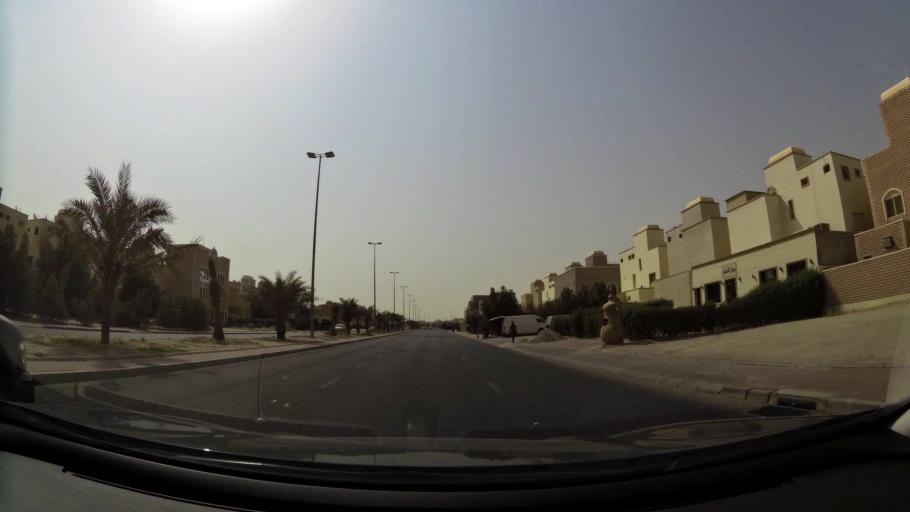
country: KW
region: Muhafazat al Jahra'
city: Al Jahra'
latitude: 29.3166
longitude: 47.7287
